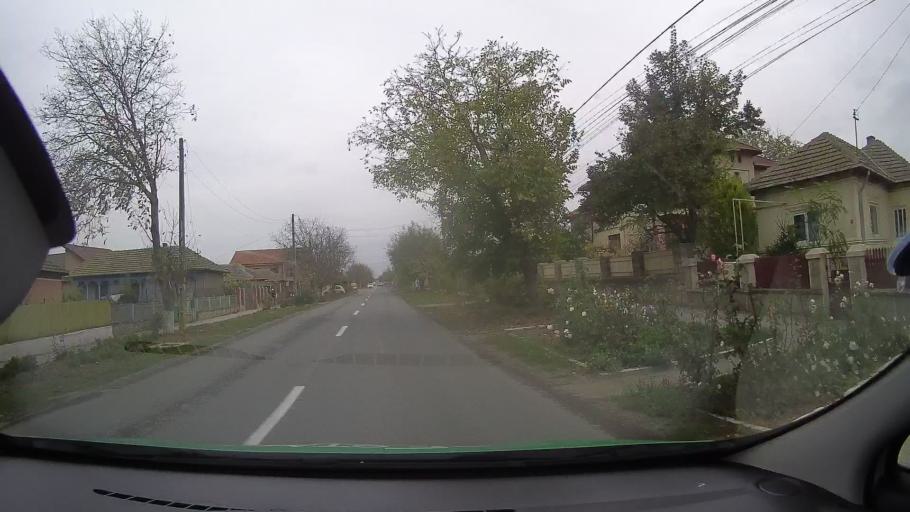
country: RO
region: Constanta
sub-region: Comuna Mihail Kogalniceanu
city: Mihail Kogalniceanu
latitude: 44.3681
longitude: 28.4627
